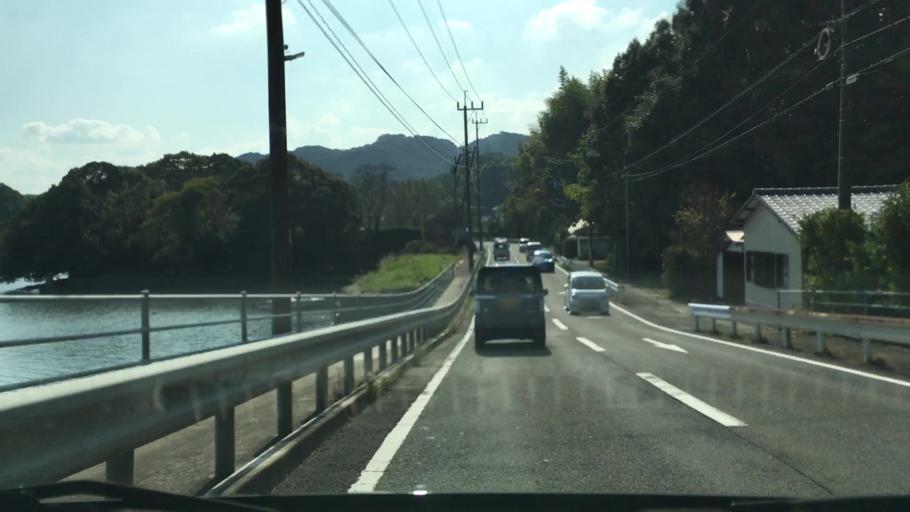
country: JP
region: Nagasaki
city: Togitsu
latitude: 32.9358
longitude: 129.7839
